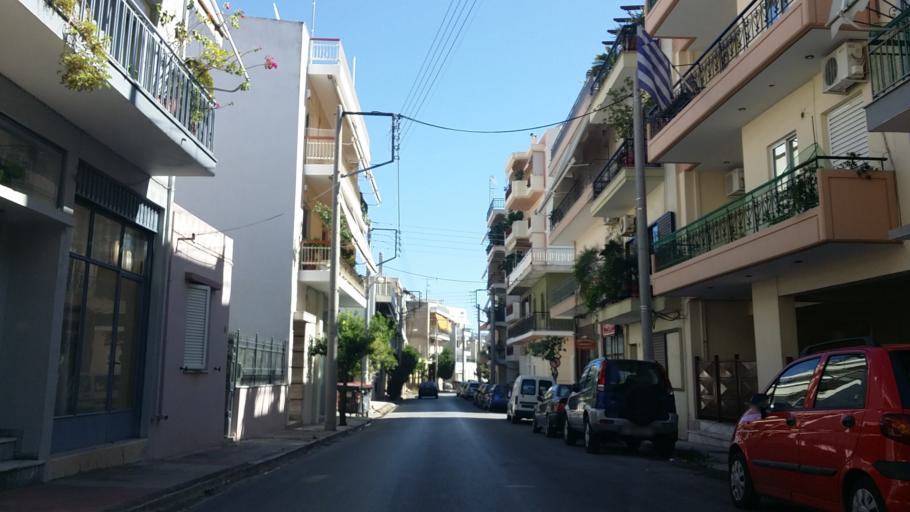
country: GR
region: Attica
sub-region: Nomarchia Athinas
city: Peristeri
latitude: 38.0230
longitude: 23.6922
